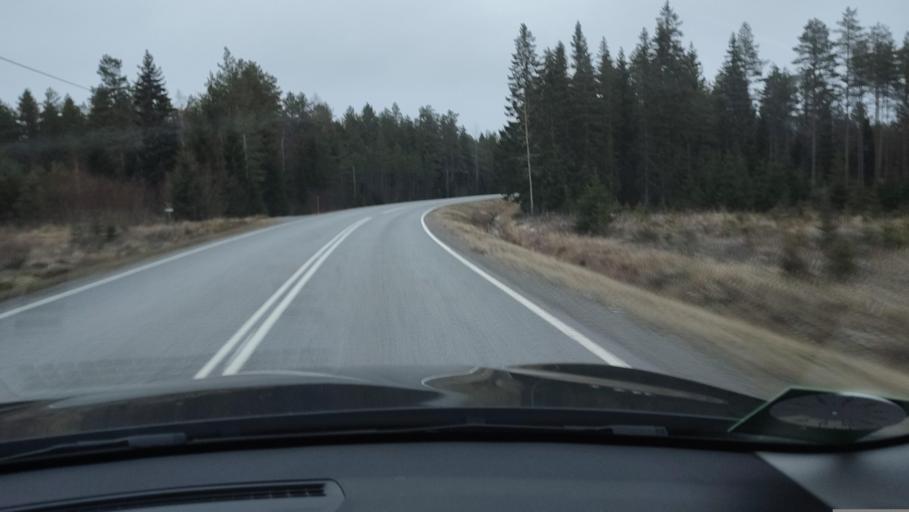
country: FI
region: Southern Ostrobothnia
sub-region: Suupohja
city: Isojoki
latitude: 62.3426
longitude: 21.9488
